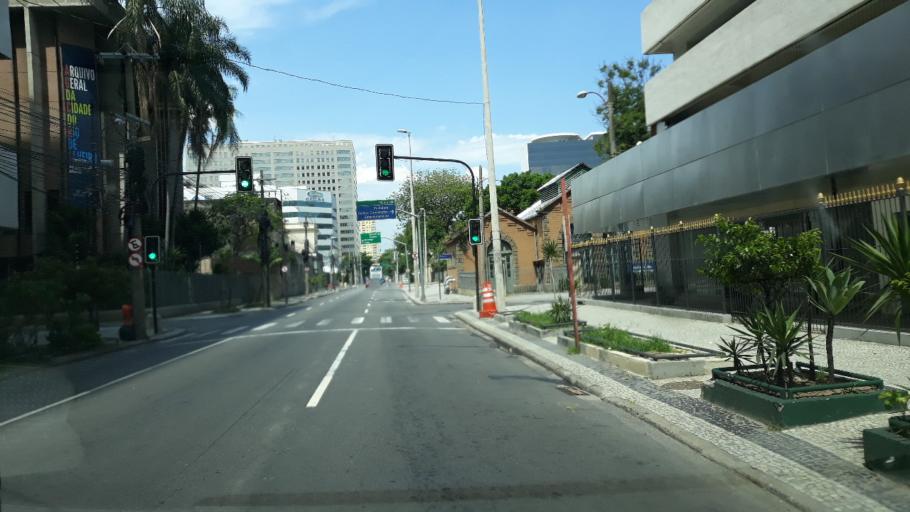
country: BR
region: Rio de Janeiro
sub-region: Rio De Janeiro
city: Rio de Janeiro
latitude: -22.9099
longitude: -43.2026
